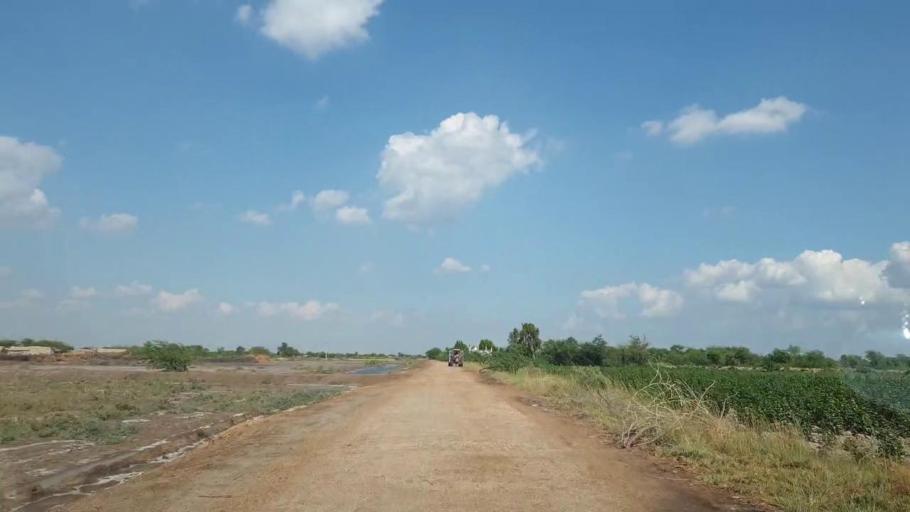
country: PK
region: Sindh
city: Pithoro
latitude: 25.6006
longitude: 69.3905
